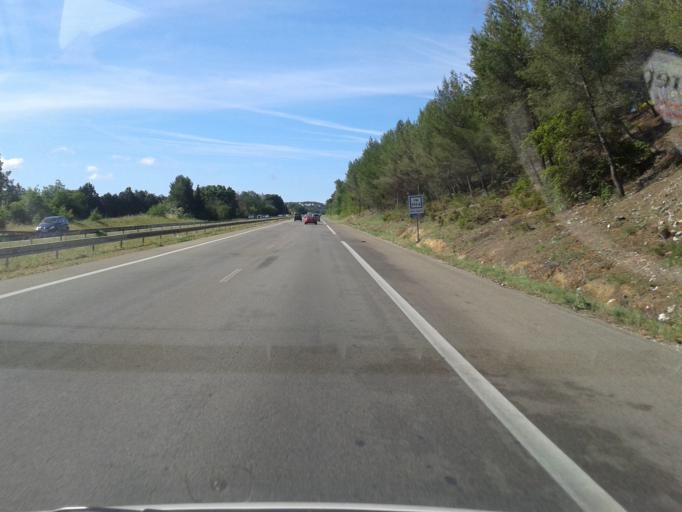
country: FR
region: Provence-Alpes-Cote d'Azur
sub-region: Departement des Bouches-du-Rhone
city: Bouc-Bel-Air
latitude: 43.4886
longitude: 5.4074
